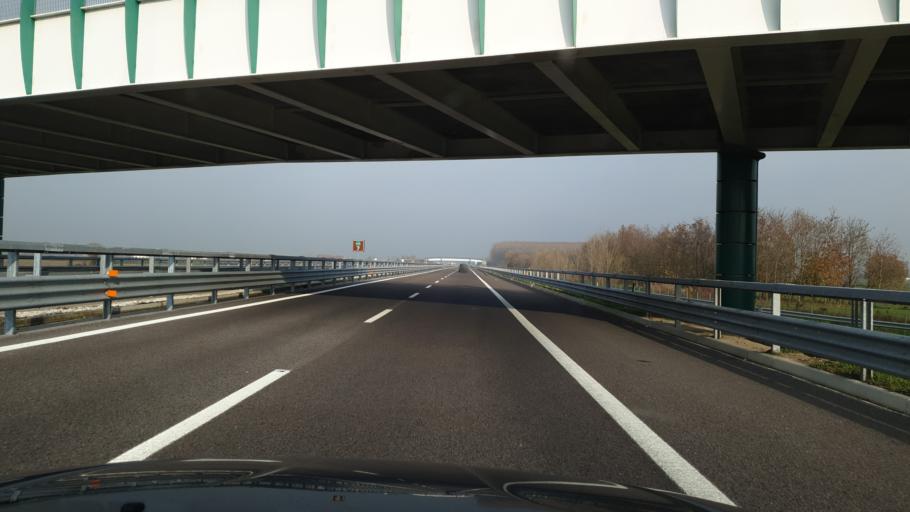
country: IT
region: Veneto
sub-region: Provincia di Padova
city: Megliadino San Vitale
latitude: 45.1848
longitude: 11.5393
